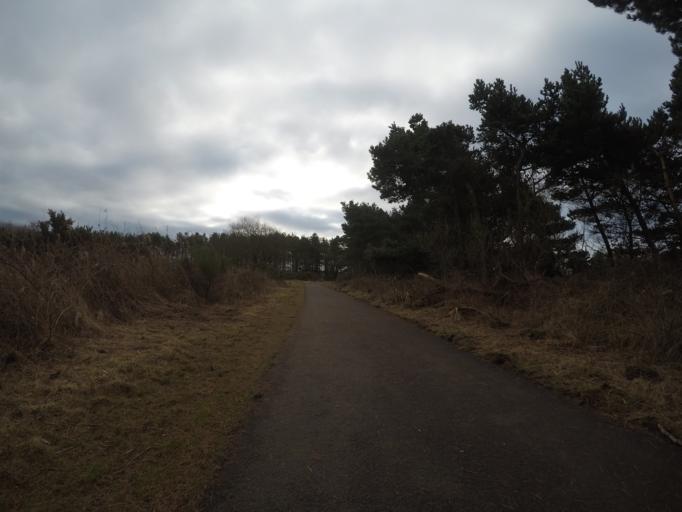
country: GB
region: Scotland
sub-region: North Ayrshire
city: Irvine
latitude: 55.5949
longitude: -4.6731
